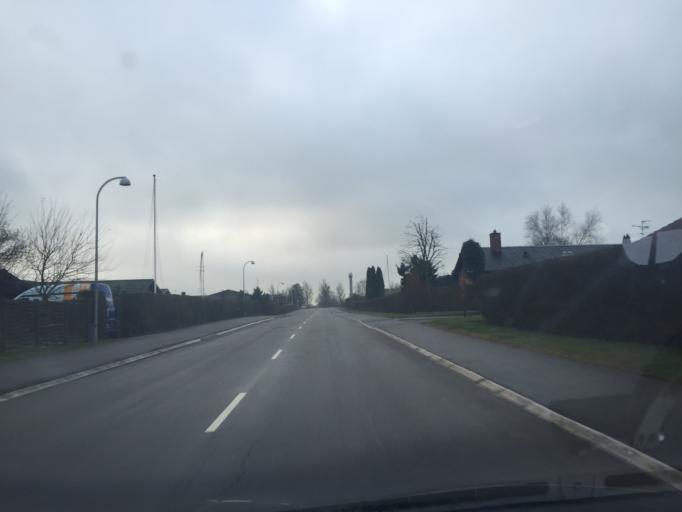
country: DK
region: Capital Region
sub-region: Hoje-Taastrup Kommune
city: Flong
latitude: 55.6823
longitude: 12.2391
